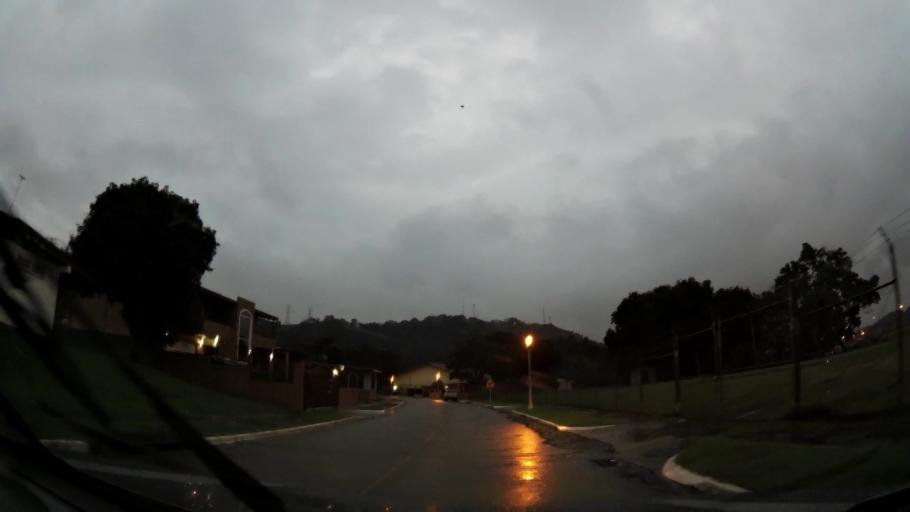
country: PA
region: Panama
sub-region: Distrito de Panama
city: Paraiso
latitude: 9.0268
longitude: -79.6232
